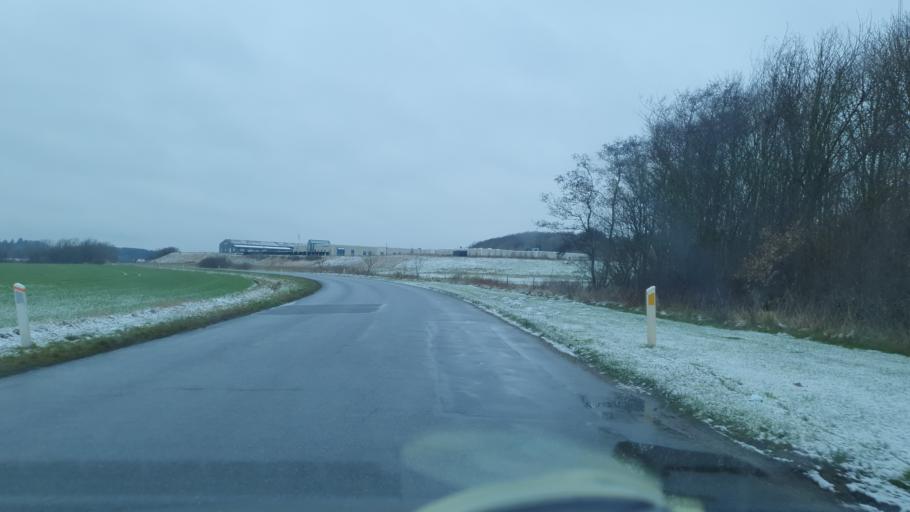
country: DK
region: North Denmark
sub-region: Jammerbugt Kommune
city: Brovst
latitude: 57.0994
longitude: 9.5092
